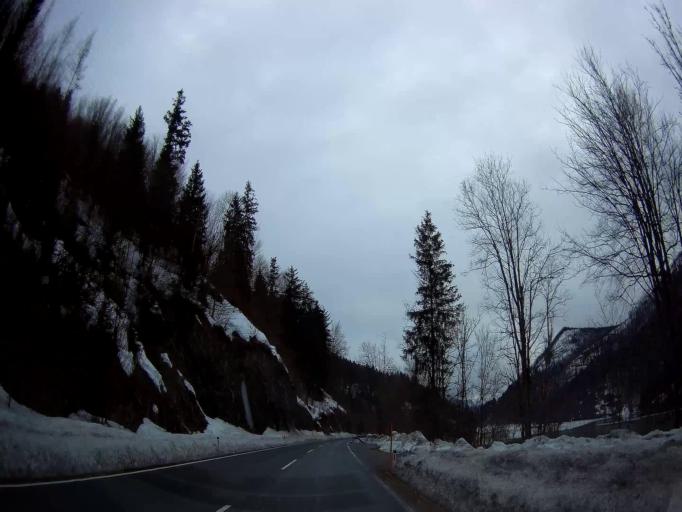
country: AT
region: Salzburg
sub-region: Politischer Bezirk Salzburg-Umgebung
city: Ebenau
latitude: 47.7567
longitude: 13.1795
